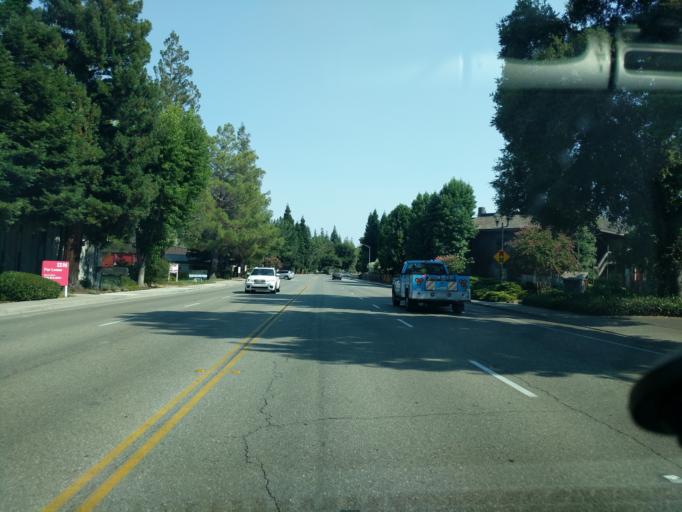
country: US
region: California
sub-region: Contra Costa County
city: Danville
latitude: 37.8100
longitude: -121.9943
